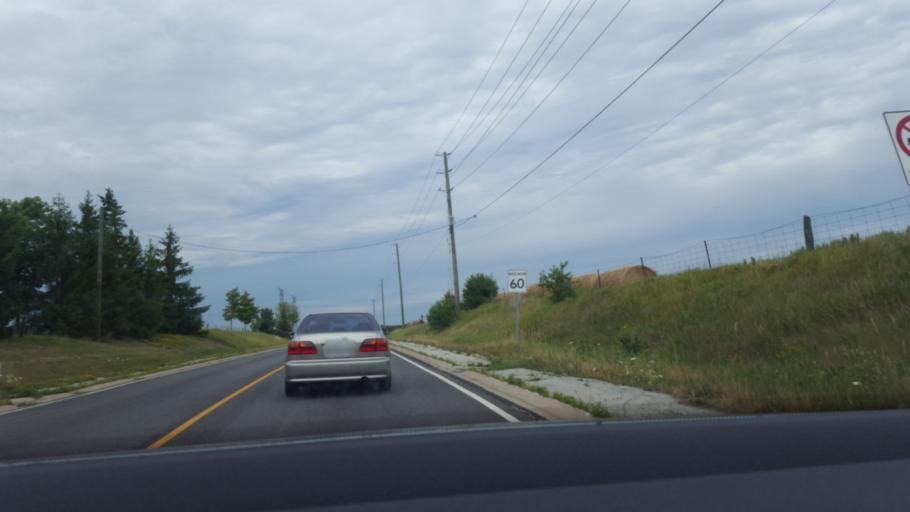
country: CA
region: Ontario
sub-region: Halton
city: Milton
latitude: 43.5593
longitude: -79.9005
